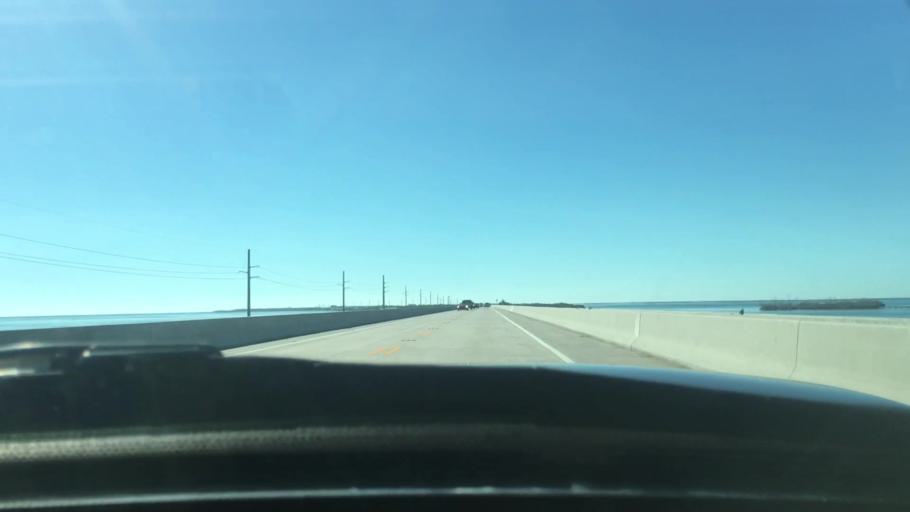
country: US
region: Florida
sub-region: Monroe County
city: Marathon
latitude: 24.6852
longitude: -81.2183
